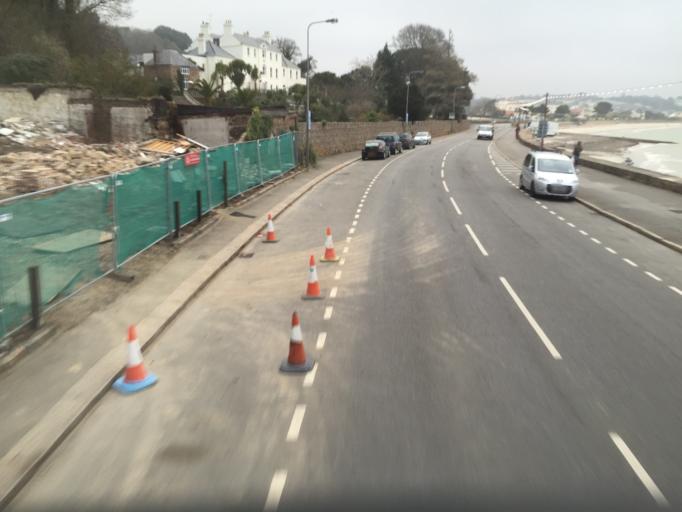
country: JE
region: St Helier
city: Saint Helier
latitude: 49.1909
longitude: -2.1683
